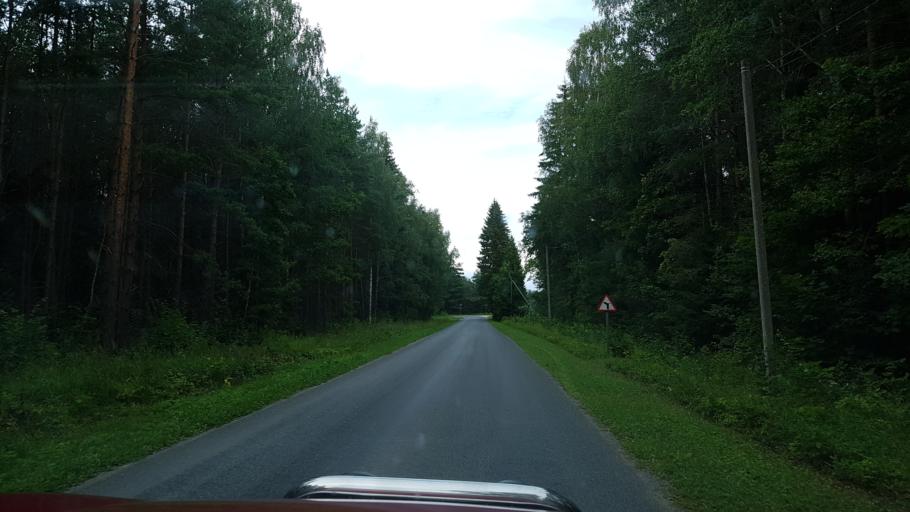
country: EE
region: Laeaene
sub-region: Ridala Parish
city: Uuemoisa
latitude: 59.0055
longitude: 23.7233
